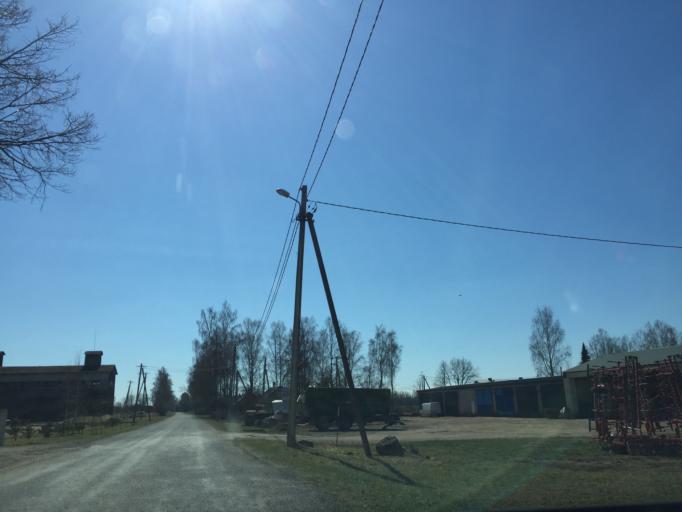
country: EE
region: Viljandimaa
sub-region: Viiratsi vald
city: Viiratsi
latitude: 58.3896
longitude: 25.7437
